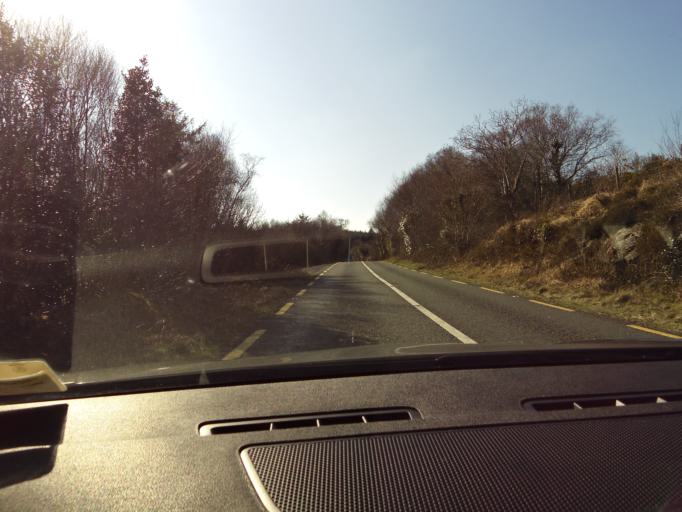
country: IE
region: Connaught
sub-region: County Galway
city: Clifden
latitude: 53.4728
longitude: -9.8729
